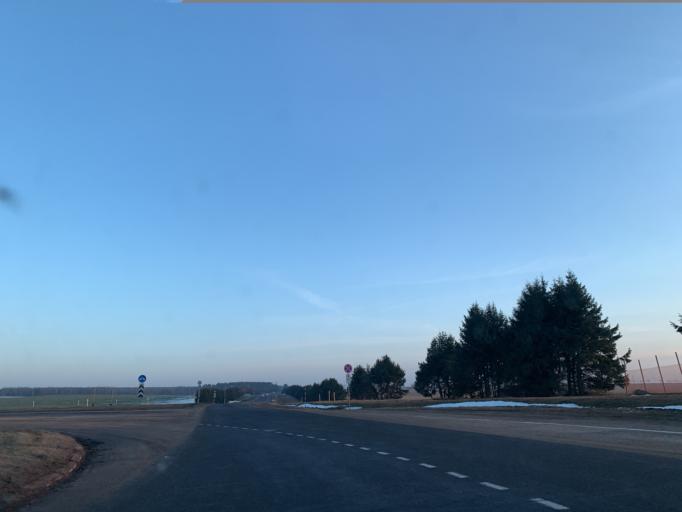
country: BY
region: Minsk
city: Haradzyeya
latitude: 53.2936
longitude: 26.5751
